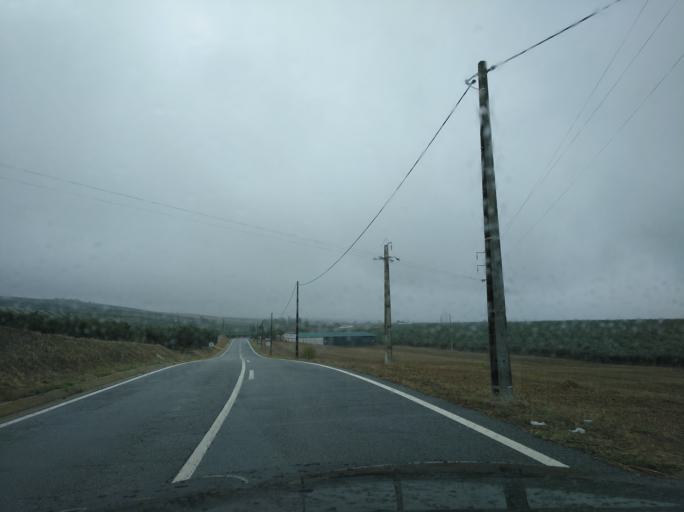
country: PT
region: Portalegre
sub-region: Campo Maior
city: Campo Maior
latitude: 38.9988
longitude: -7.0718
